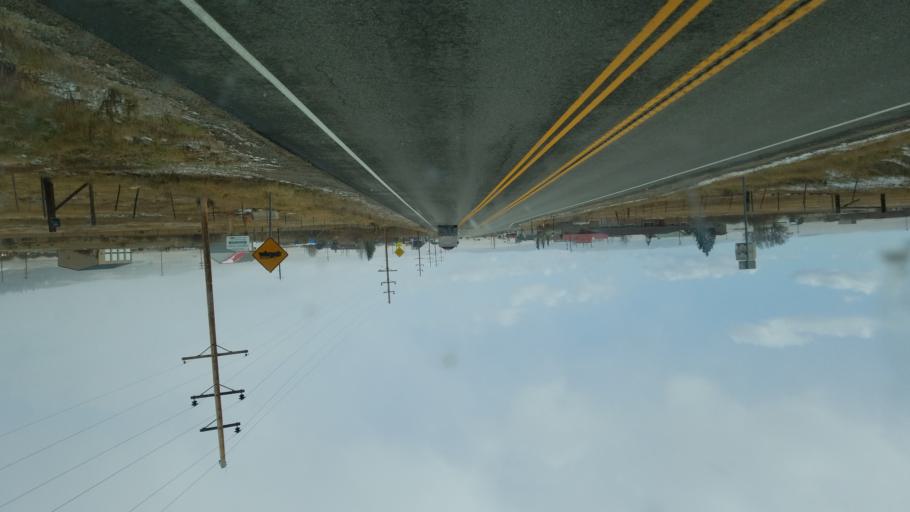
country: US
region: Colorado
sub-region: Park County
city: Fairplay
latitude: 39.3796
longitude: -105.7979
